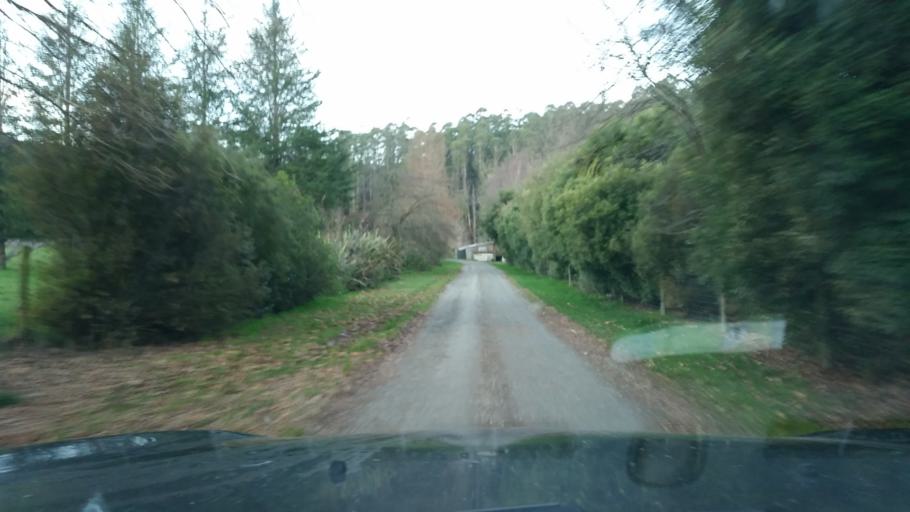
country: NZ
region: Marlborough
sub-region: Marlborough District
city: Blenheim
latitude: -41.4733
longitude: 173.7423
